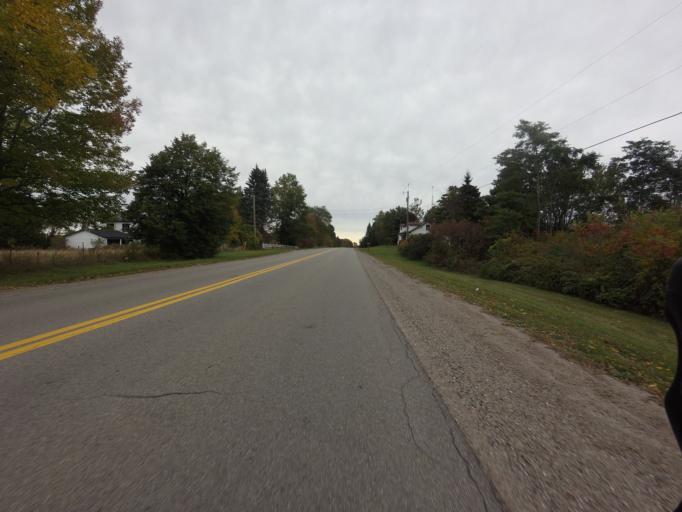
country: CA
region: Ontario
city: Gananoque
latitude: 44.4965
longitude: -76.1862
